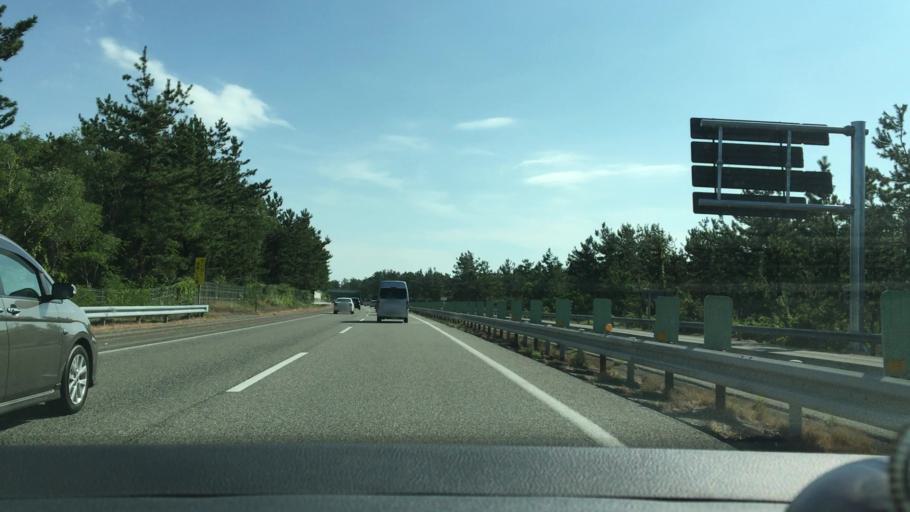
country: JP
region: Ishikawa
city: Komatsu
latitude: 36.4387
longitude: 136.4371
